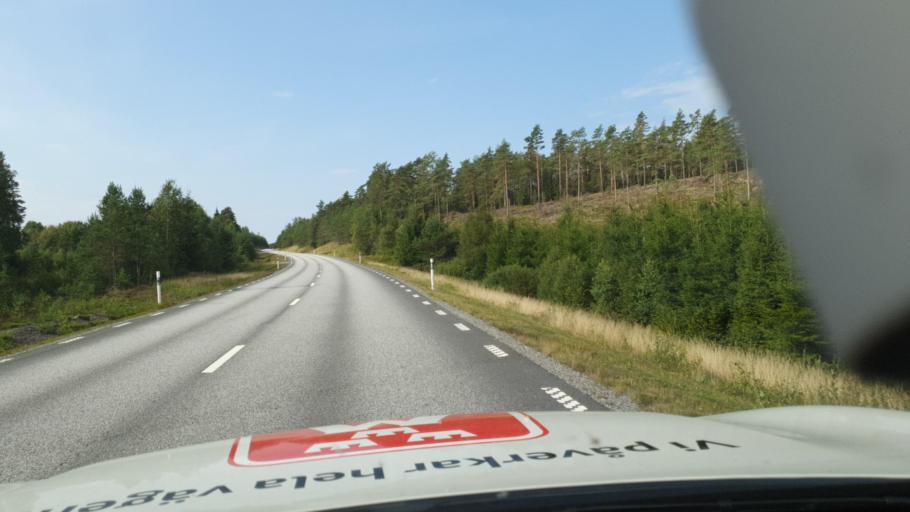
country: SE
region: Vaestra Goetaland
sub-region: Dals-Ed Kommun
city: Ed
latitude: 58.8449
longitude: 11.6674
